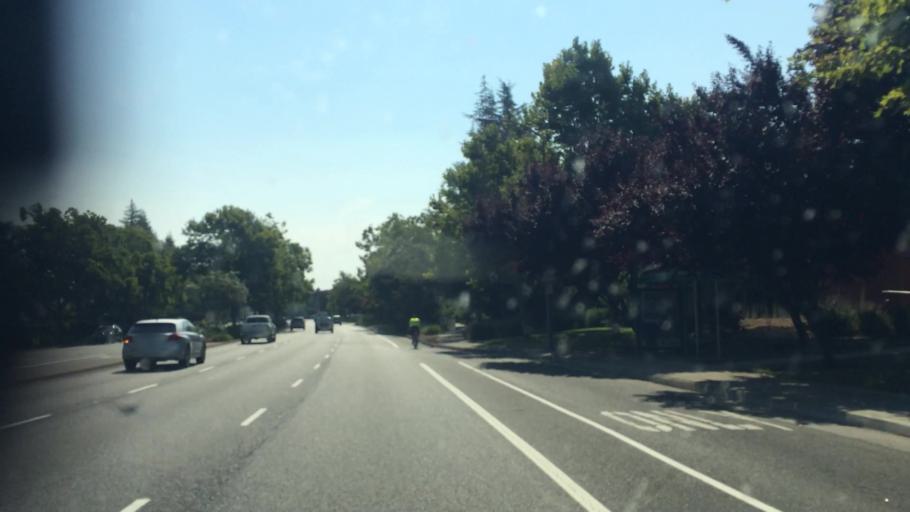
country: US
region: California
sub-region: Sacramento County
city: Laguna
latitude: 38.4232
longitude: -121.4525
